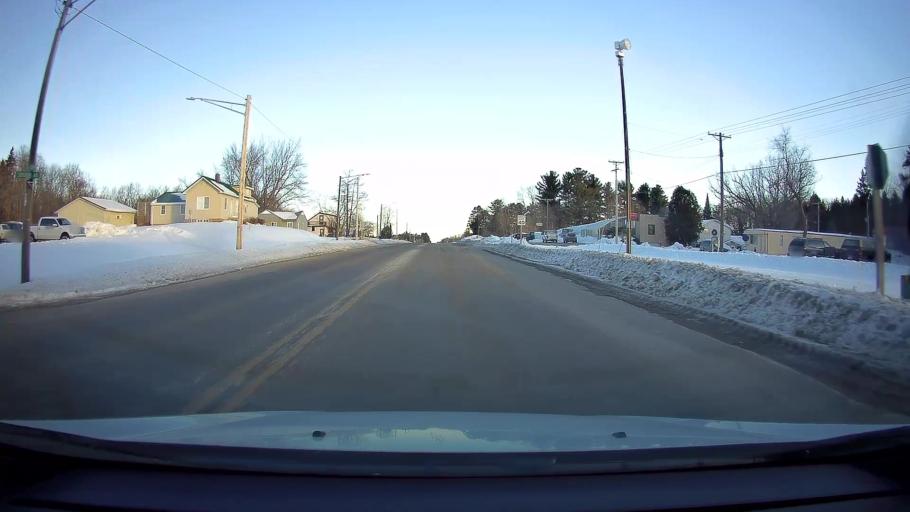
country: US
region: Wisconsin
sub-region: Barron County
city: Cumberland
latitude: 45.5470
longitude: -92.0171
